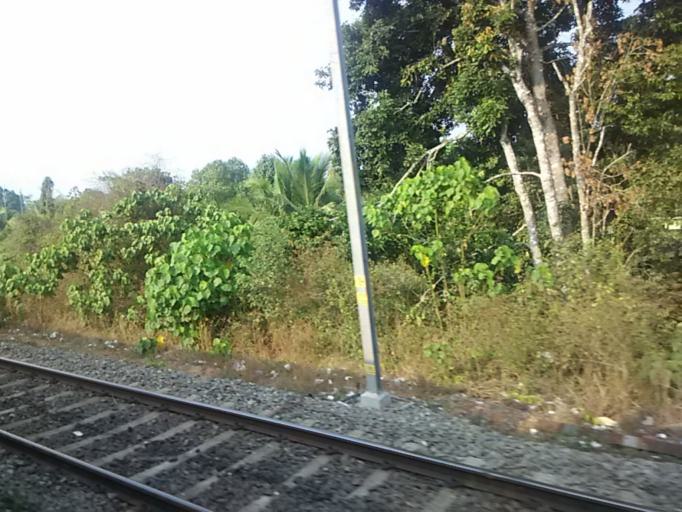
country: IN
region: Kerala
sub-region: Malappuram
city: Pariyapuram
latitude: 11.0360
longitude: 75.8658
